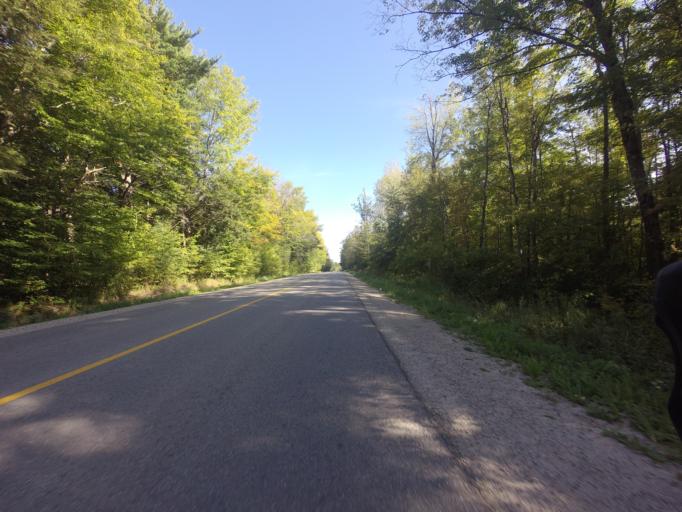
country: CA
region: Ontario
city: Perth
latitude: 44.8959
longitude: -76.3250
